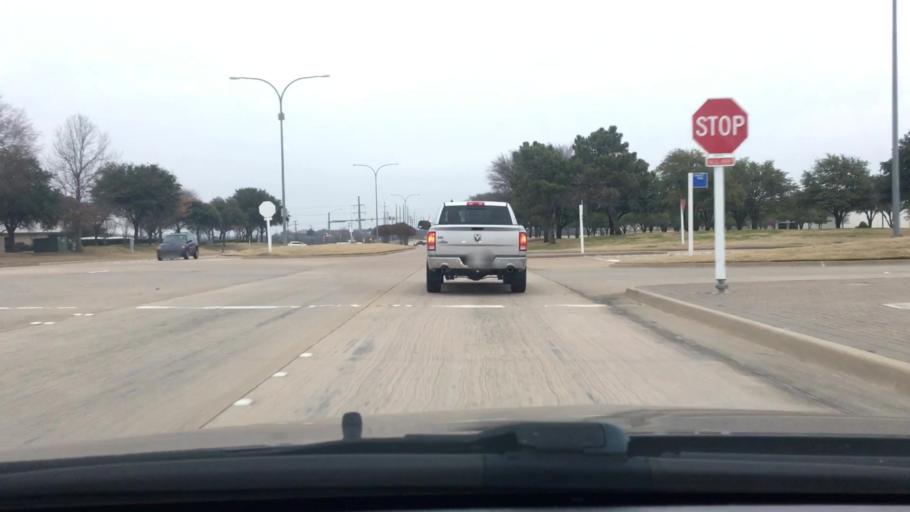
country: US
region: Texas
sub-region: Tarrant County
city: Keller
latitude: 32.9766
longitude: -97.2627
